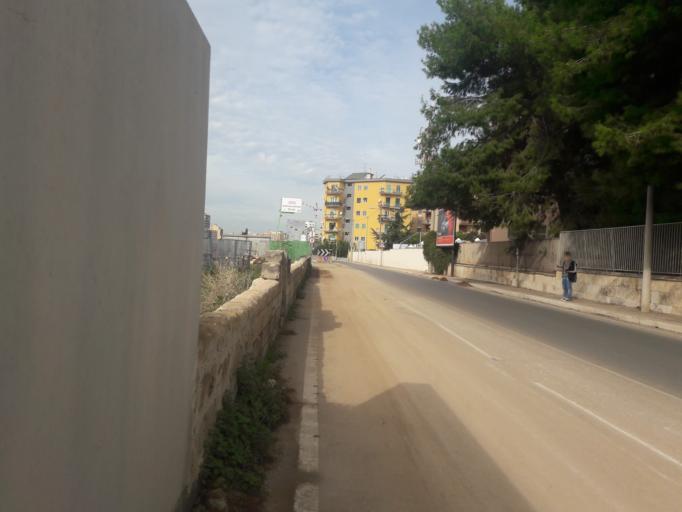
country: IT
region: Apulia
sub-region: Provincia di Bari
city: Bari
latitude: 41.1128
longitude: 16.8877
